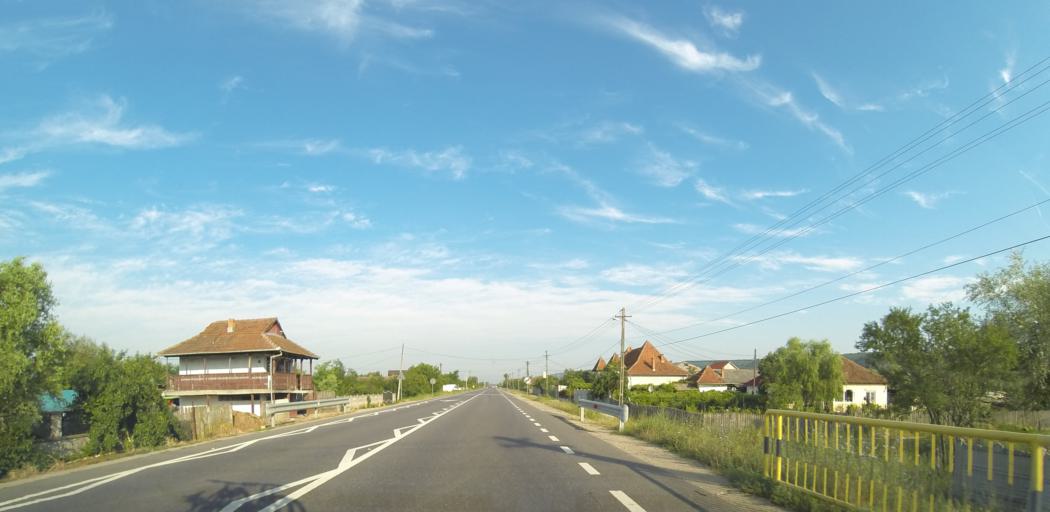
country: RO
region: Gorj
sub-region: Comuna Ionesti
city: Ionesti
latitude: 44.5751
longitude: 23.4146
